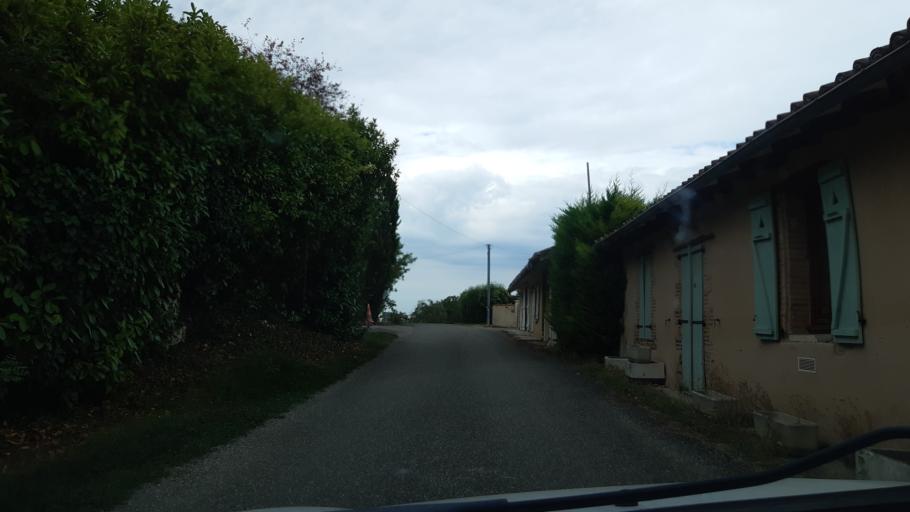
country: FR
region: Midi-Pyrenees
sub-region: Departement du Gers
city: Gimont
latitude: 43.7003
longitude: 0.9958
